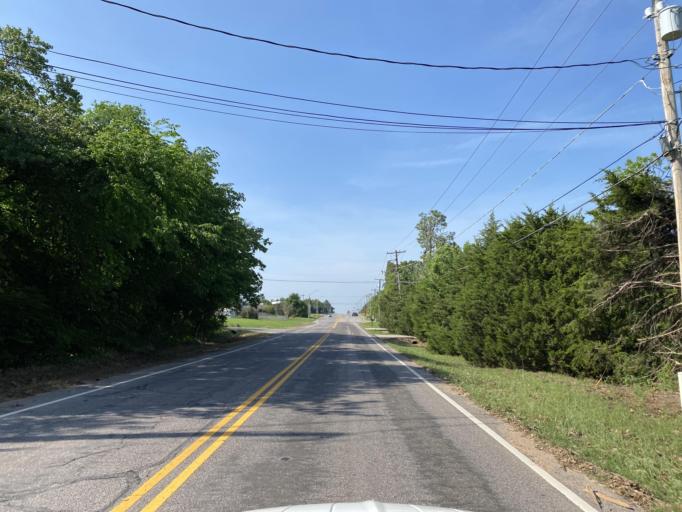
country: US
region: Oklahoma
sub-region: Oklahoma County
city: Nicoma Park
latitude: 35.4614
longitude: -97.3357
